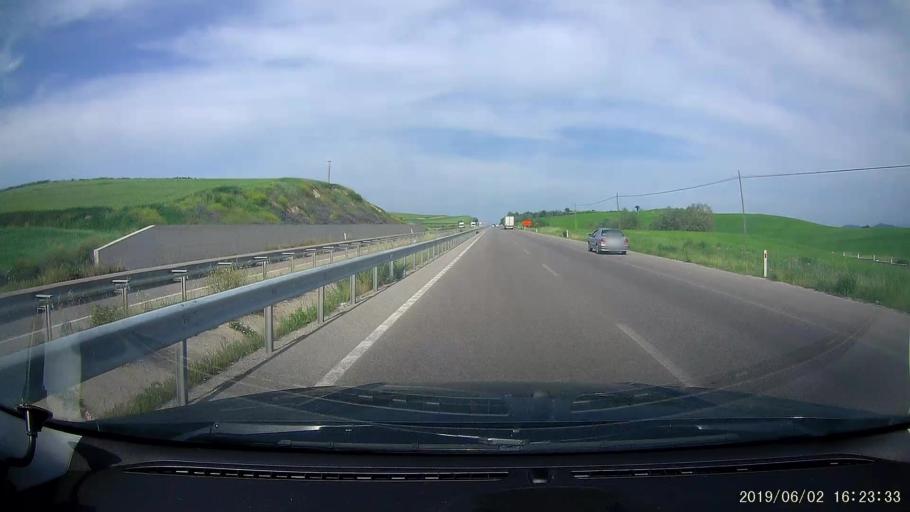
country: TR
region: Samsun
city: Havza
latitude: 40.9949
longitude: 35.7385
